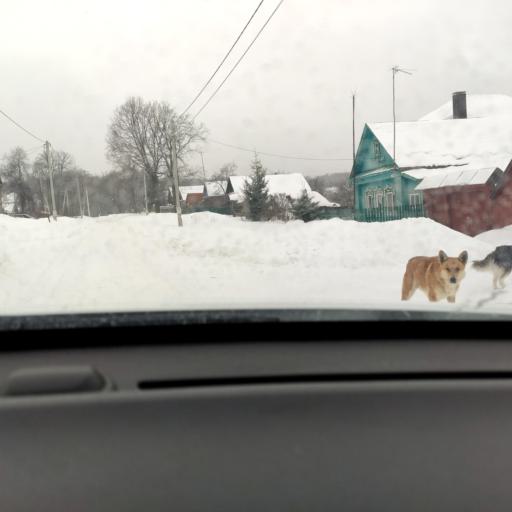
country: RU
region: Tatarstan
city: Stolbishchi
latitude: 55.6739
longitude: 49.1142
